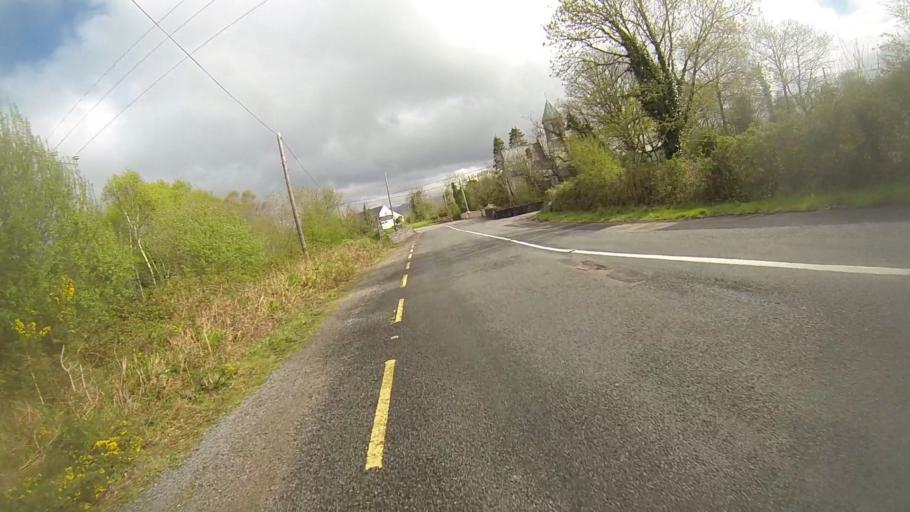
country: IE
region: Munster
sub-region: Ciarrai
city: Kenmare
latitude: 51.8312
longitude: -9.8237
